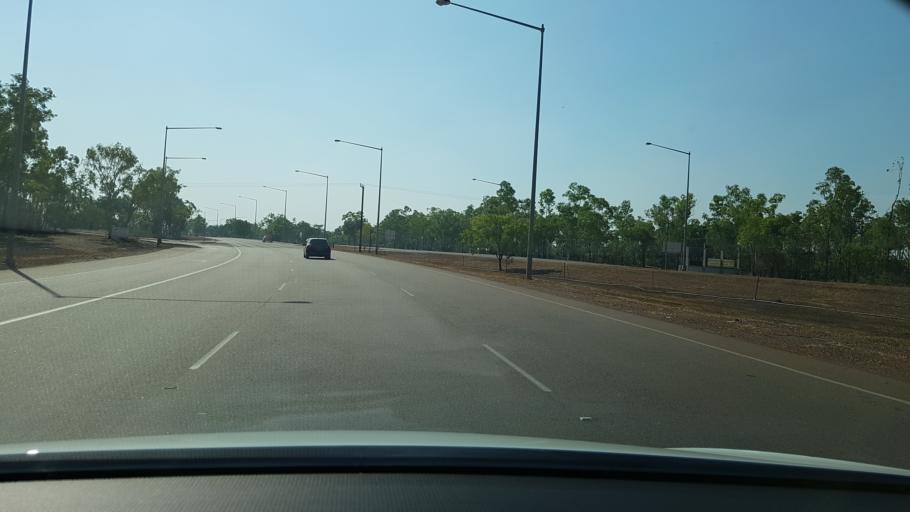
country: AU
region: Northern Territory
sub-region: Palmerston
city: Palmerston
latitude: -12.4626
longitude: 130.9741
